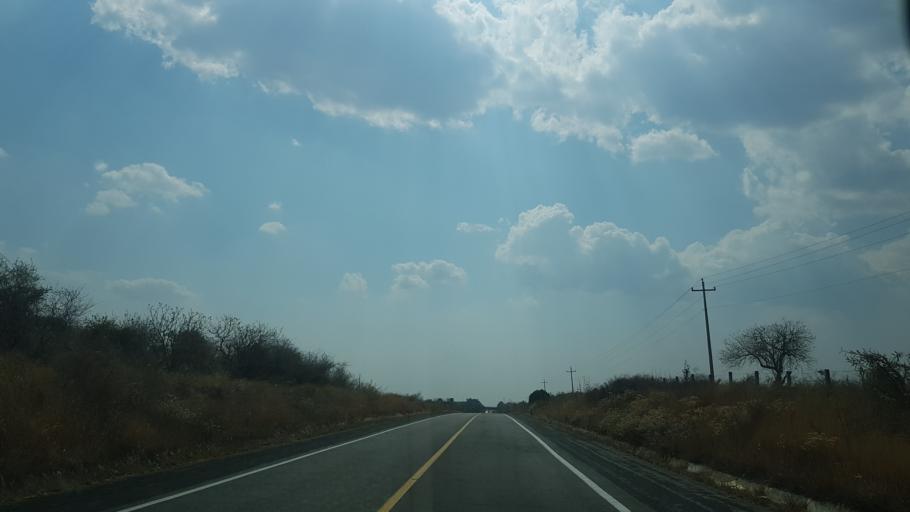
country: MX
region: Puebla
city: San Juan Amecac
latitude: 18.8169
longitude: -98.6563
